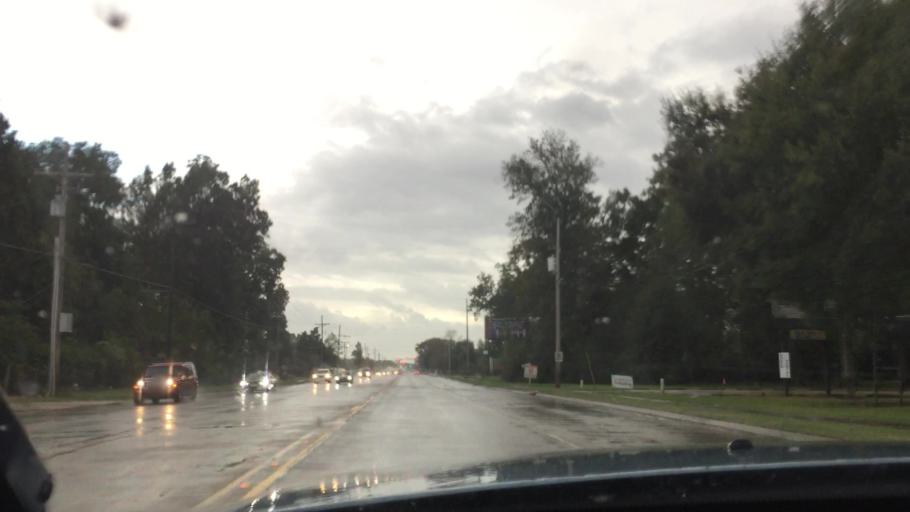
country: US
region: Louisiana
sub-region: East Baton Rouge Parish
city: Monticello
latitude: 30.4505
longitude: -91.0246
